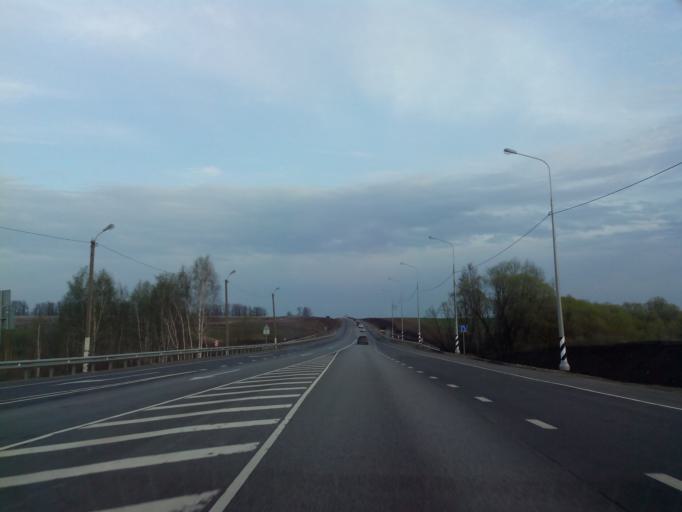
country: RU
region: Rjazan
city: Ryazhsk
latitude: 53.5561
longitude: 40.0537
